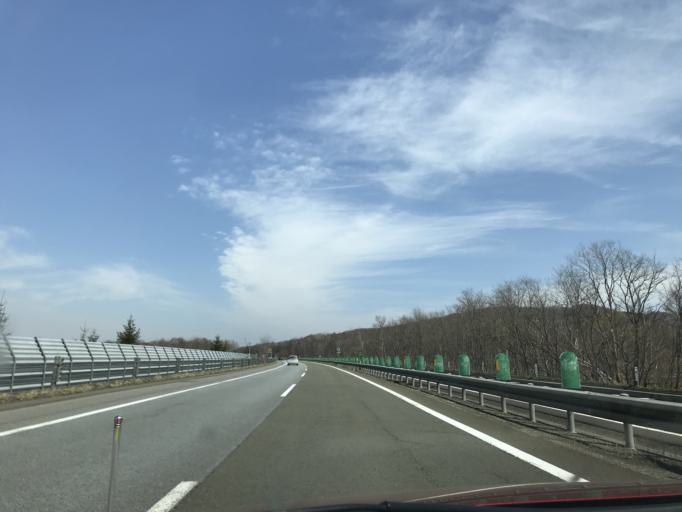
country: JP
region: Hokkaido
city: Bibai
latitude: 43.2690
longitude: 141.8456
